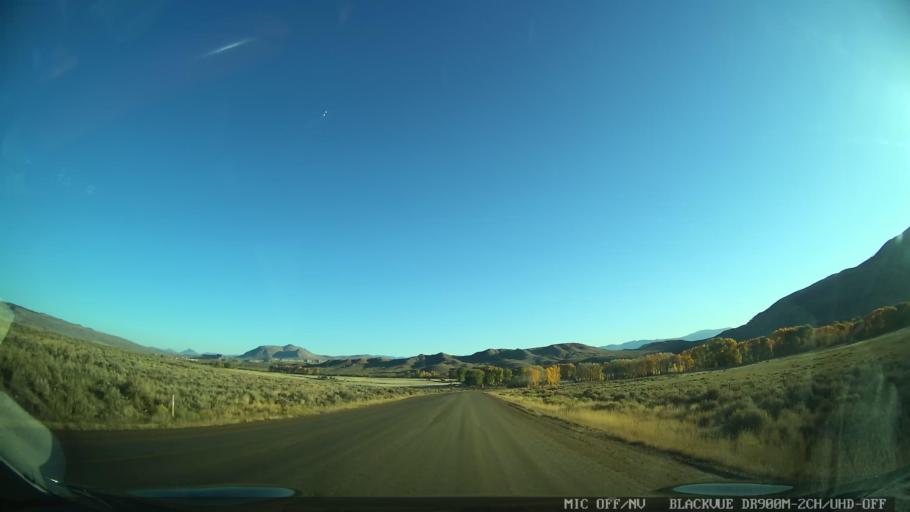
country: US
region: Colorado
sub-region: Grand County
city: Kremmling
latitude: 40.0257
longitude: -106.3891
